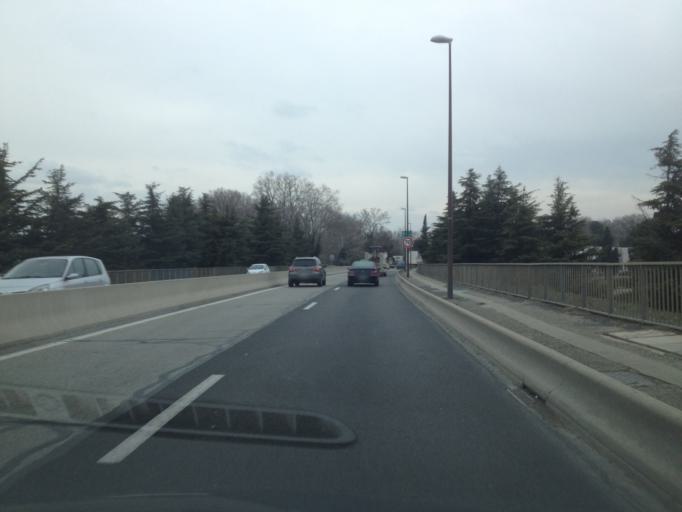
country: FR
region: Provence-Alpes-Cote d'Azur
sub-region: Departement du Vaucluse
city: Avignon
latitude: 43.9387
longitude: 4.8321
